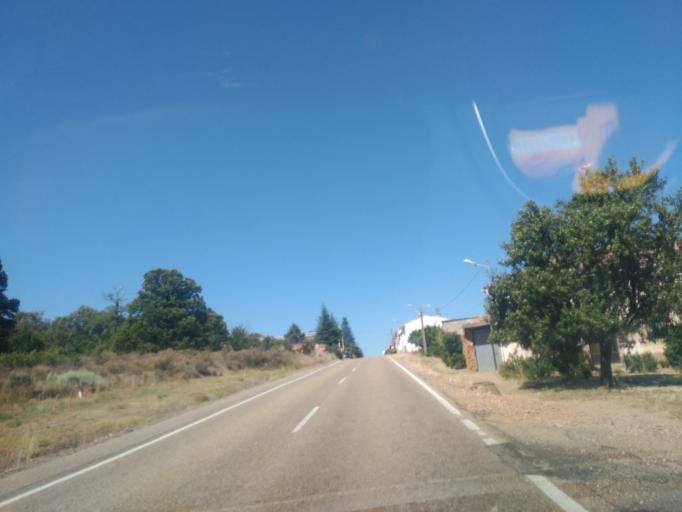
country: ES
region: Castille and Leon
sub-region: Provincia de Zamora
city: Otero de Bodas
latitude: 41.9364
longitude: -6.1463
